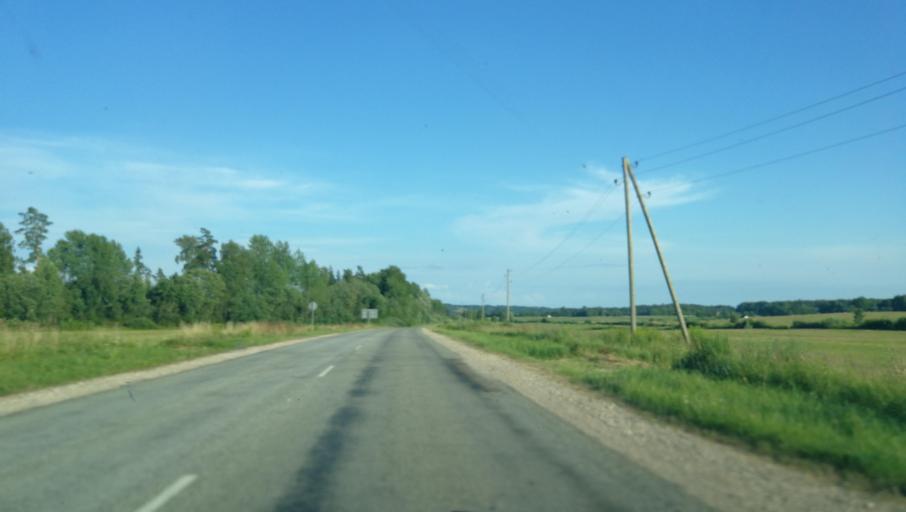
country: LV
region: Cesu Rajons
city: Cesis
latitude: 57.2923
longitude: 25.3070
